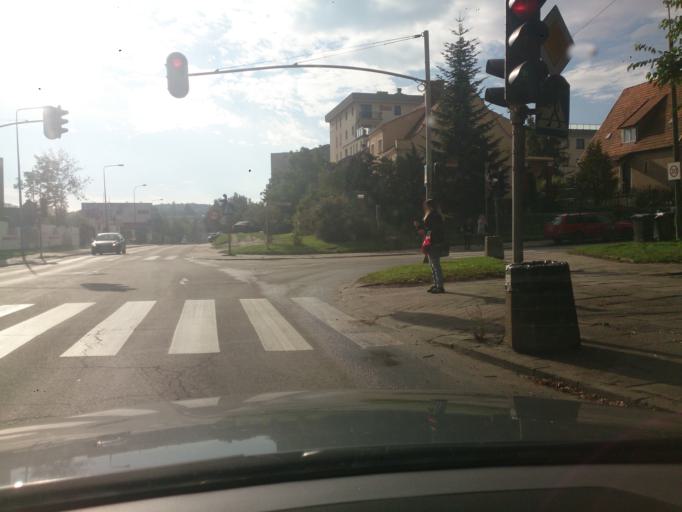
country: PL
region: Pomeranian Voivodeship
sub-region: Sopot
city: Sopot
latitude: 54.3825
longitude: 18.5854
